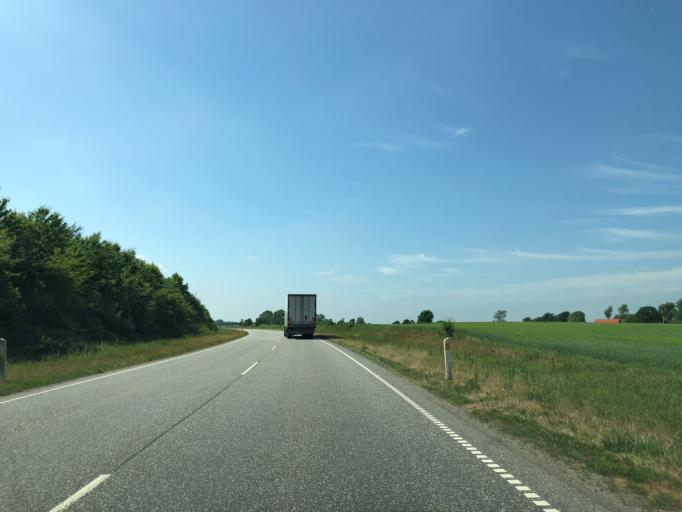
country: DK
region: South Denmark
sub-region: Kolding Kommune
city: Kolding
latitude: 55.5462
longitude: 9.4729
